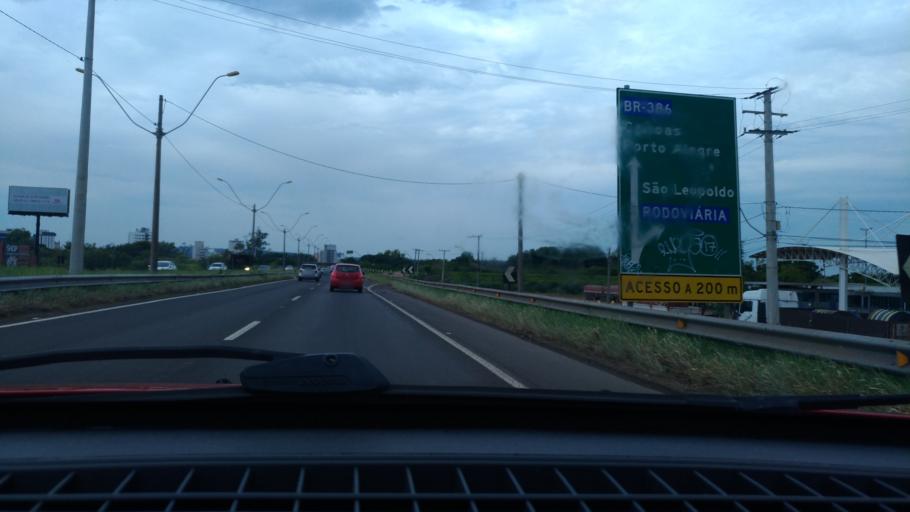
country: BR
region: Rio Grande do Sul
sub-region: Sao Leopoldo
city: Sao Leopoldo
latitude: -29.7553
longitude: -51.1518
